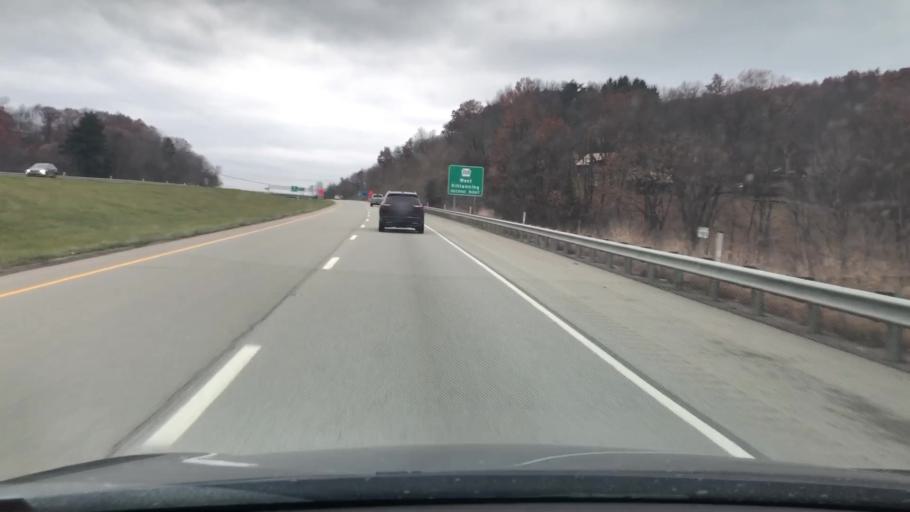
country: US
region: Pennsylvania
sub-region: Armstrong County
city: West Kittanning
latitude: 40.8067
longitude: -79.5394
